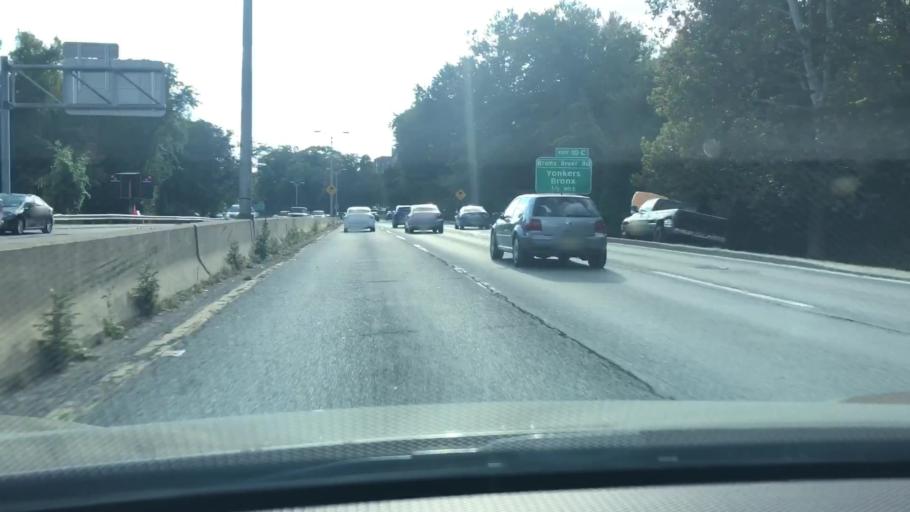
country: US
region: New York
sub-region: Westchester County
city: Mount Vernon
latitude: 40.9099
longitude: -73.8541
